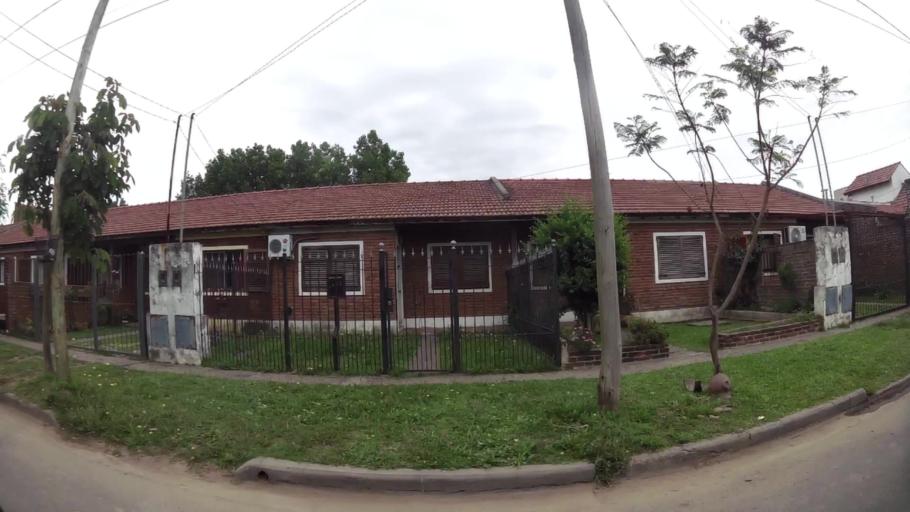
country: AR
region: Buenos Aires
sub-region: Partido de Campana
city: Campana
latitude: -34.1934
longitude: -58.9469
